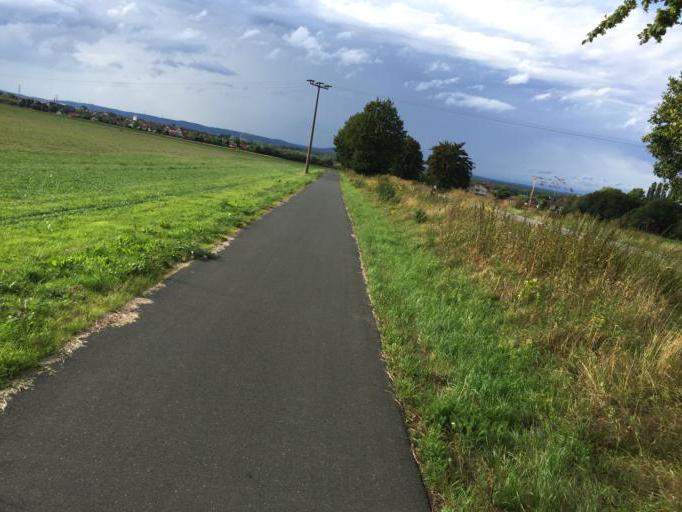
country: DE
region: Hesse
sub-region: Regierungsbezirk Giessen
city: Langgons
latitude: 50.5168
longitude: 8.6771
